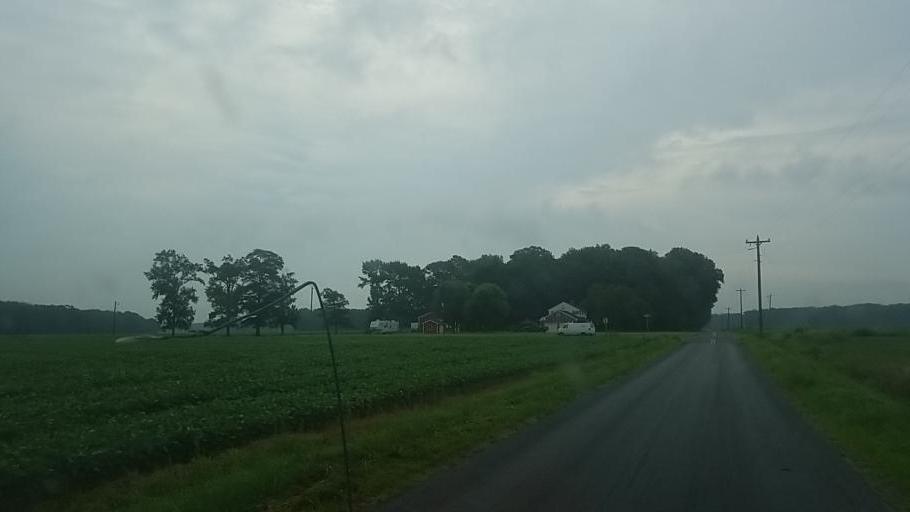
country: US
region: Delaware
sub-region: Sussex County
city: Selbyville
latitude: 38.4419
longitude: -75.2642
